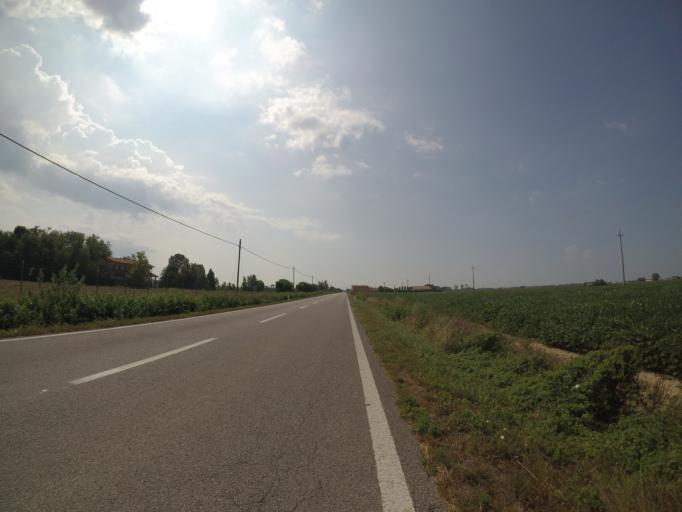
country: IT
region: Friuli Venezia Giulia
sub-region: Provincia di Udine
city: Pertegada
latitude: 45.7450
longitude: 13.0615
